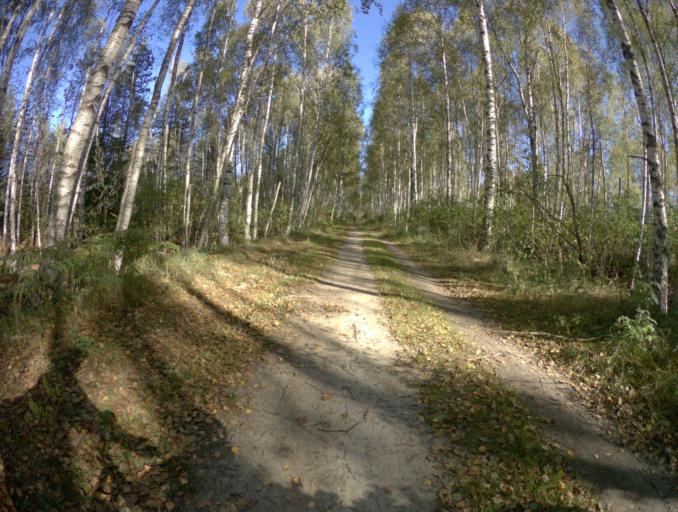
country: RU
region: Vladimir
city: Raduzhnyy
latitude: 55.9066
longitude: 40.2154
